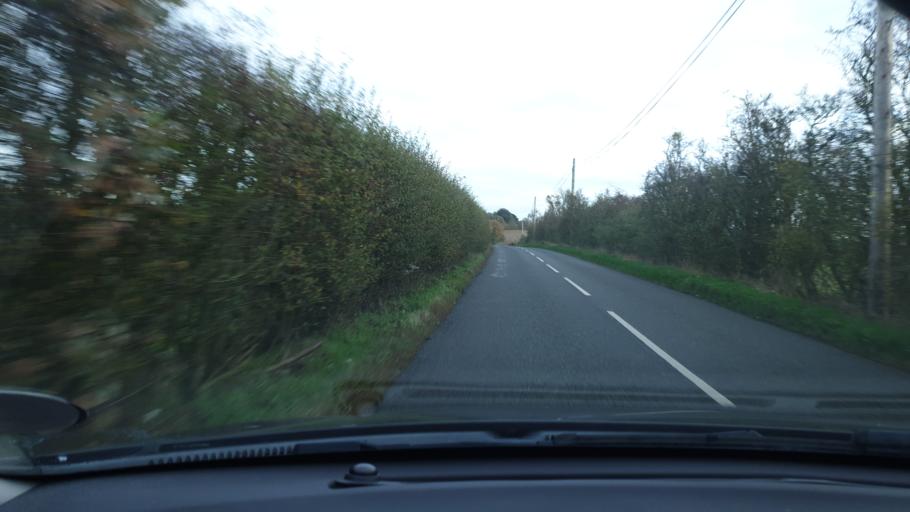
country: GB
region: England
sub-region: Essex
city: Mistley
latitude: 51.9263
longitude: 1.1194
